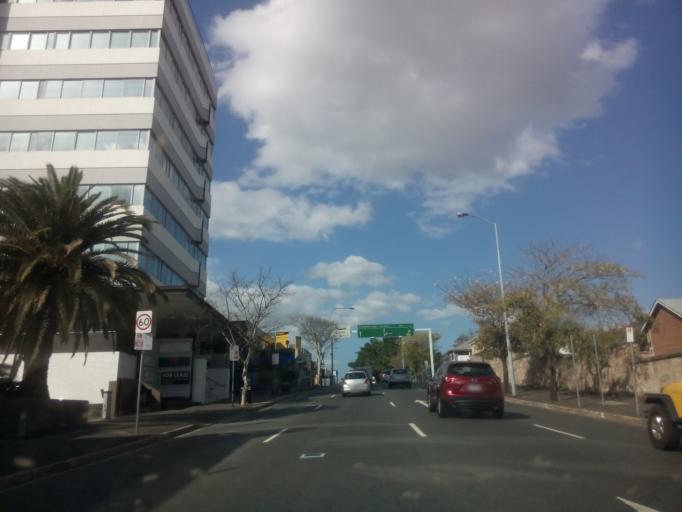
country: AU
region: Queensland
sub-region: Brisbane
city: Spring Hill
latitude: -27.4648
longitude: 153.0134
